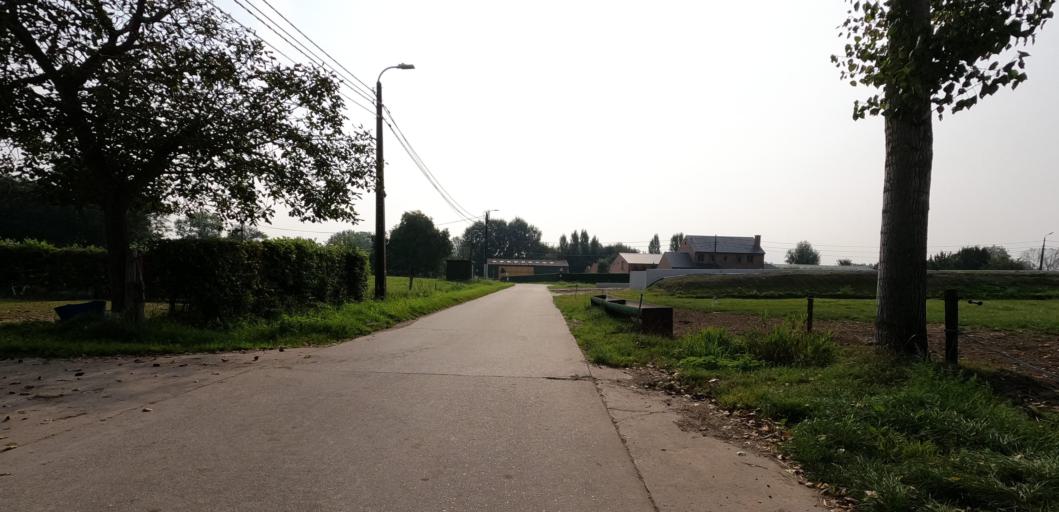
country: BE
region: Flanders
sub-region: Provincie Oost-Vlaanderen
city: Temse
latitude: 51.1542
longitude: 4.2559
